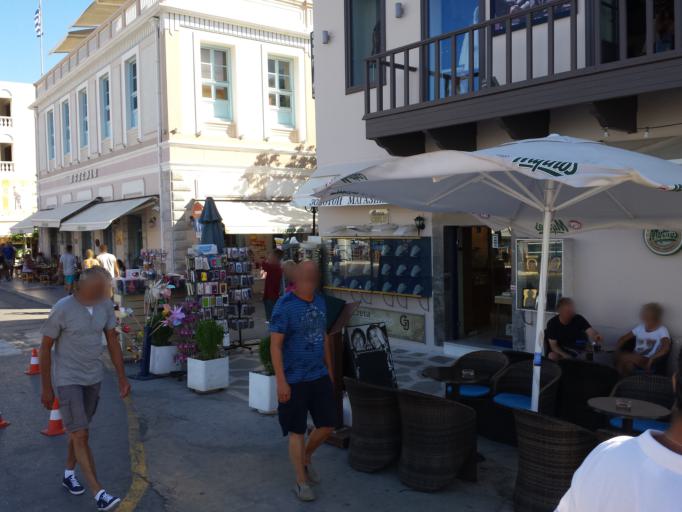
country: GR
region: Crete
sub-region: Nomos Lasithiou
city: Agios Nikolaos
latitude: 35.1908
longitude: 25.7188
